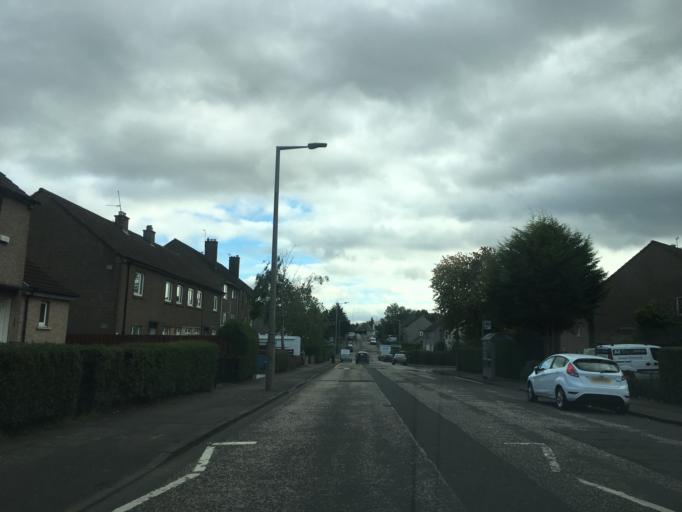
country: GB
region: Scotland
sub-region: Edinburgh
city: Edinburgh
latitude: 55.9632
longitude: -3.2485
